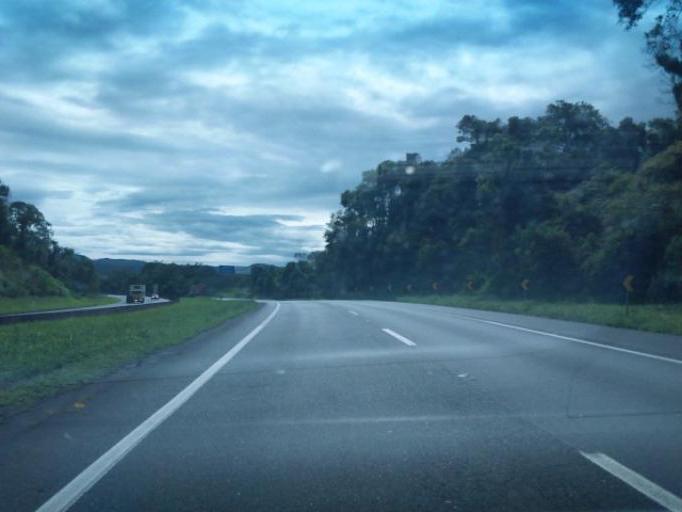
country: BR
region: Sao Paulo
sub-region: Cajati
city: Cajati
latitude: -24.9687
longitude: -48.3948
